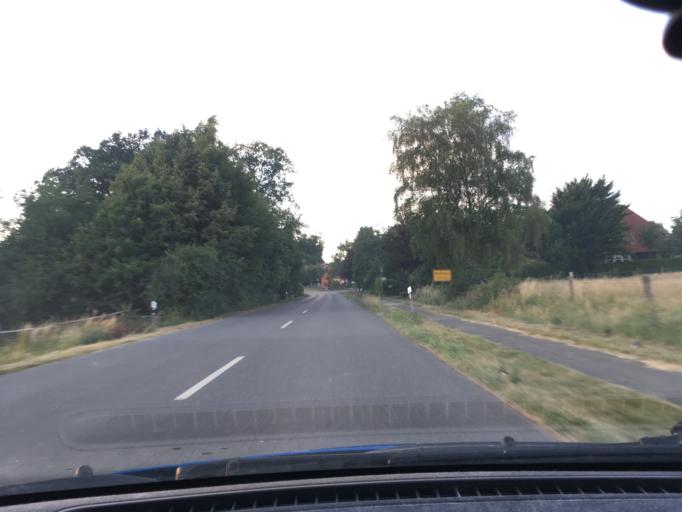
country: DE
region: Lower Saxony
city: Soderstorf
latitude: 53.1603
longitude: 10.1584
